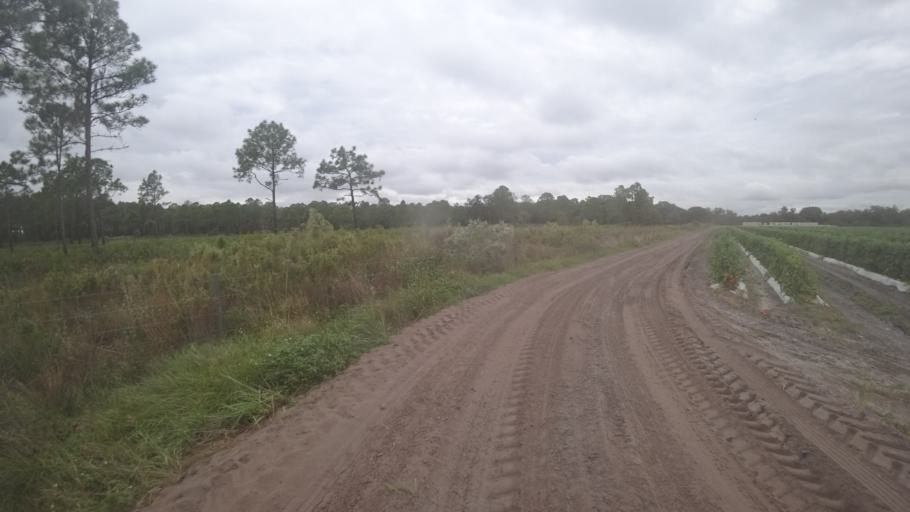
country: US
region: Florida
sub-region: Hillsborough County
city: Wimauma
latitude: 27.5675
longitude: -82.1375
